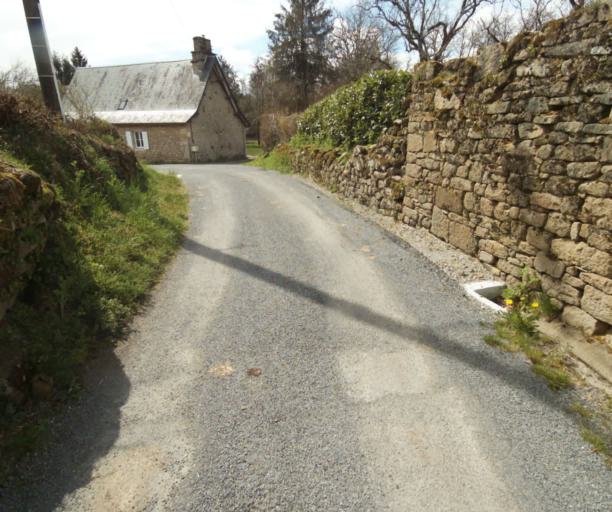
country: FR
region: Limousin
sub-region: Departement de la Correze
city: Correze
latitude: 45.3501
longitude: 1.9657
